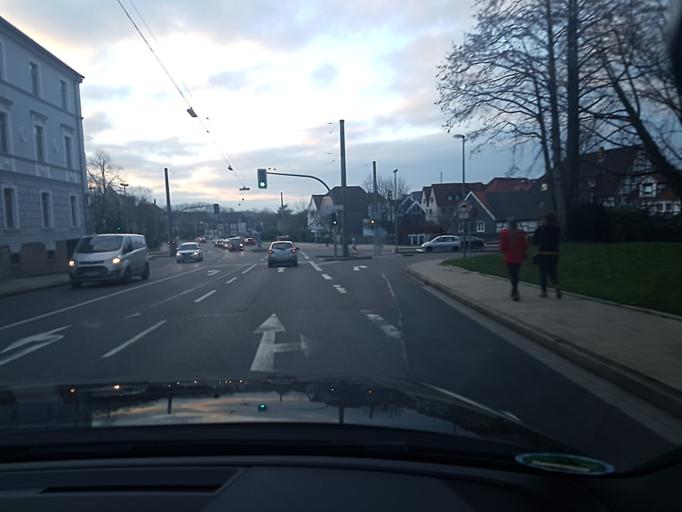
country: DE
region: North Rhine-Westphalia
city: Hattingen
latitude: 51.3965
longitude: 7.1870
